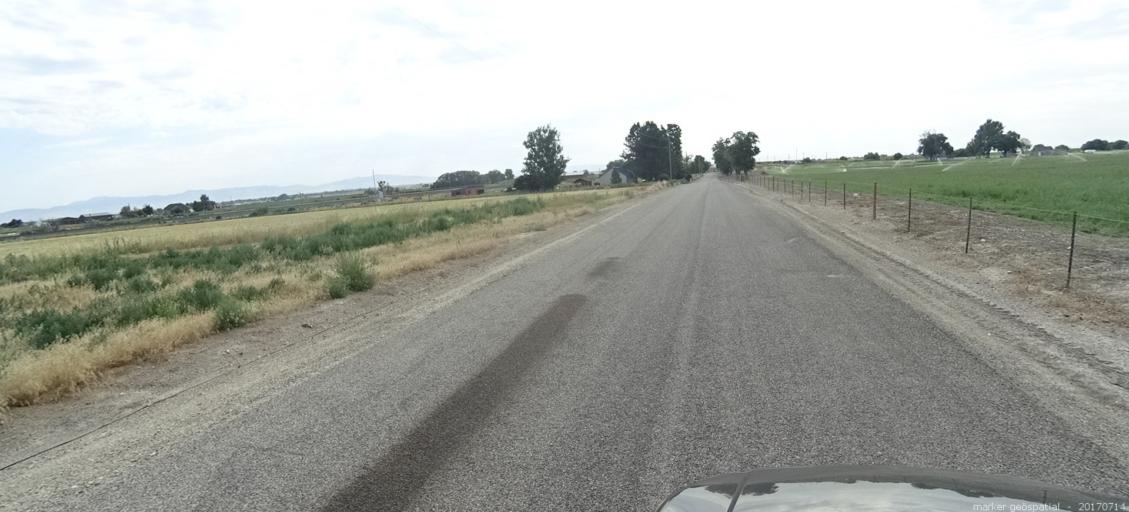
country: US
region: Idaho
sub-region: Ada County
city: Kuna
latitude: 43.4593
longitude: -116.3615
